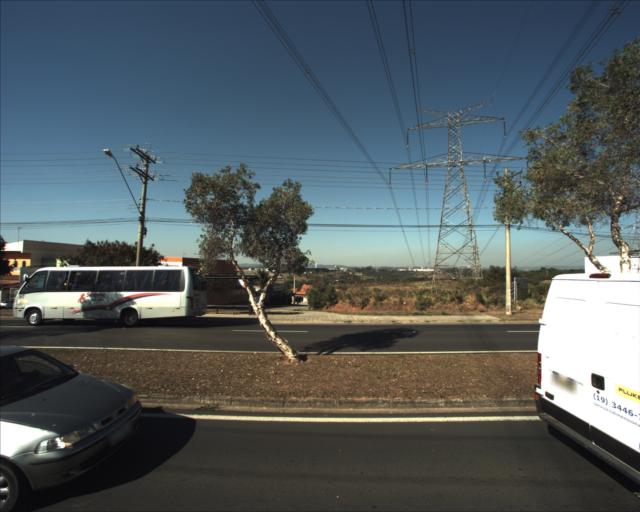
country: BR
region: Sao Paulo
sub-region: Sorocaba
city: Sorocaba
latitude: -23.4279
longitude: -47.4150
